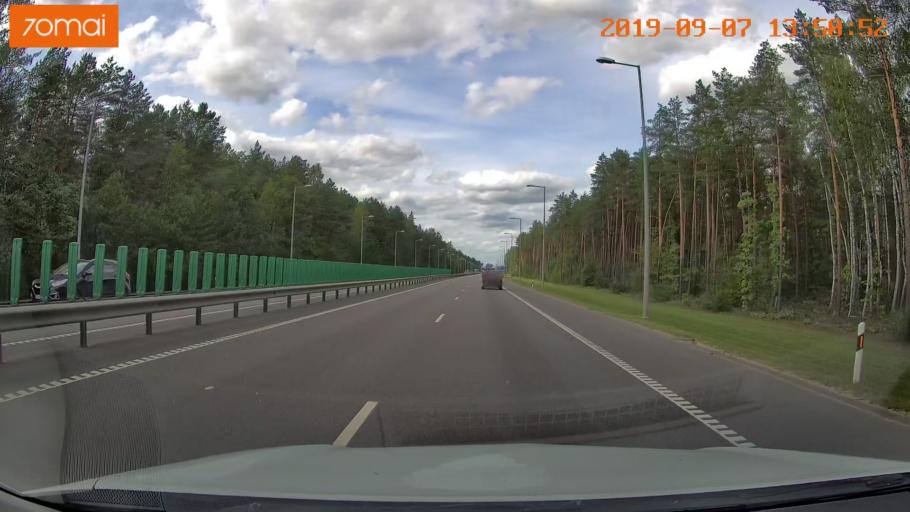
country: LT
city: Baltoji Voke
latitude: 54.6111
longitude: 25.1764
